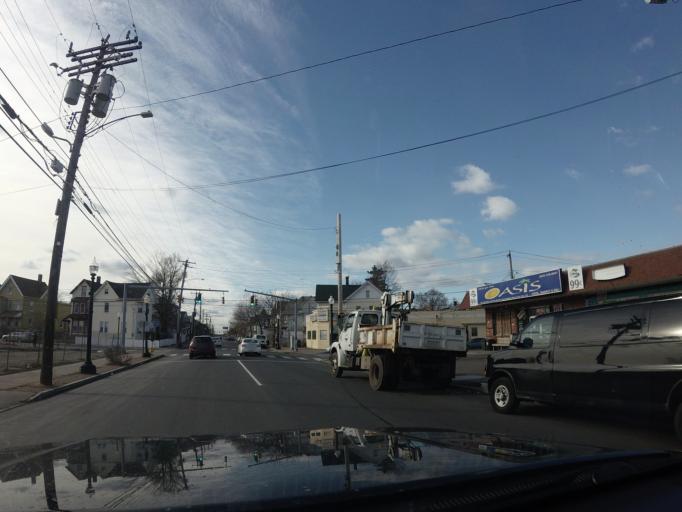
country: US
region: Connecticut
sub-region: Fairfield County
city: Stratford
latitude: 41.1803
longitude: -73.1656
